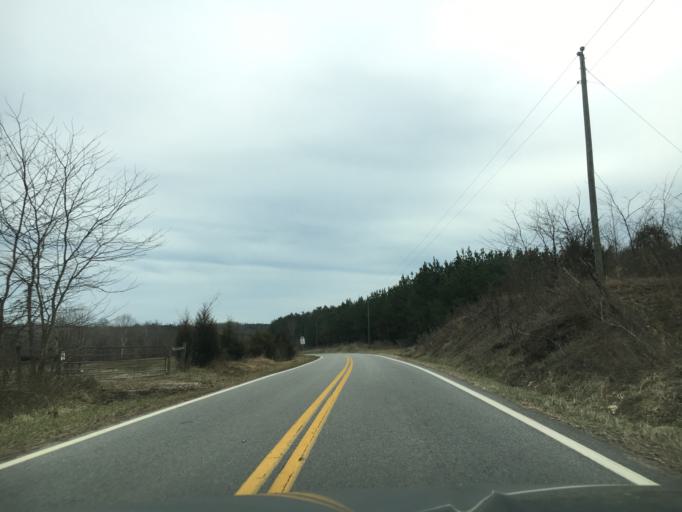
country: US
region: Virginia
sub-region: Charlotte County
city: Charlotte Court House
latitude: 37.1549
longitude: -78.7688
